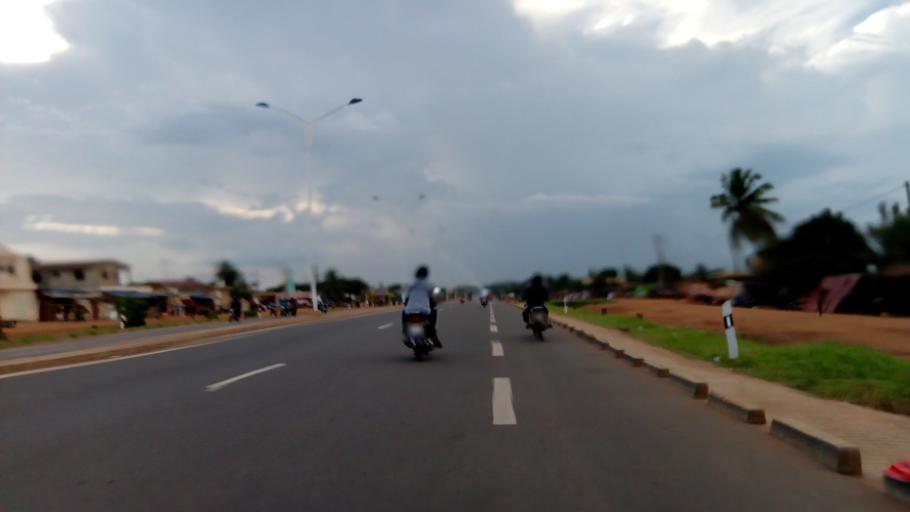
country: TG
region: Maritime
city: Lome
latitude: 6.2422
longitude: 1.1998
